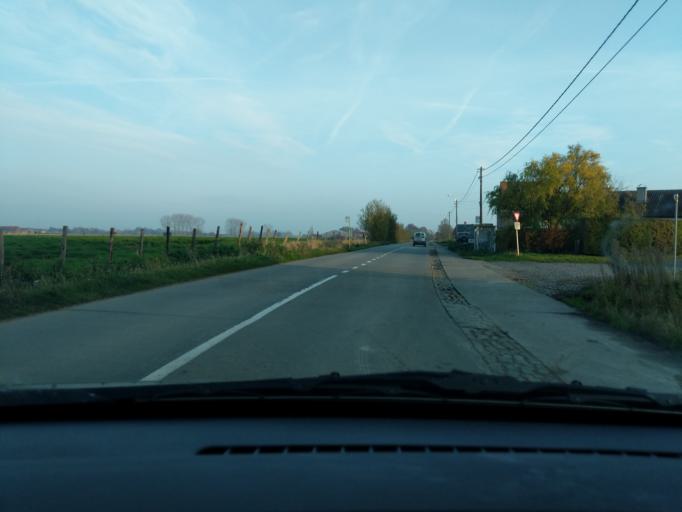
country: BE
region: Flanders
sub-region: Provincie Oost-Vlaanderen
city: Nevele
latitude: 51.0444
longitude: 3.4948
